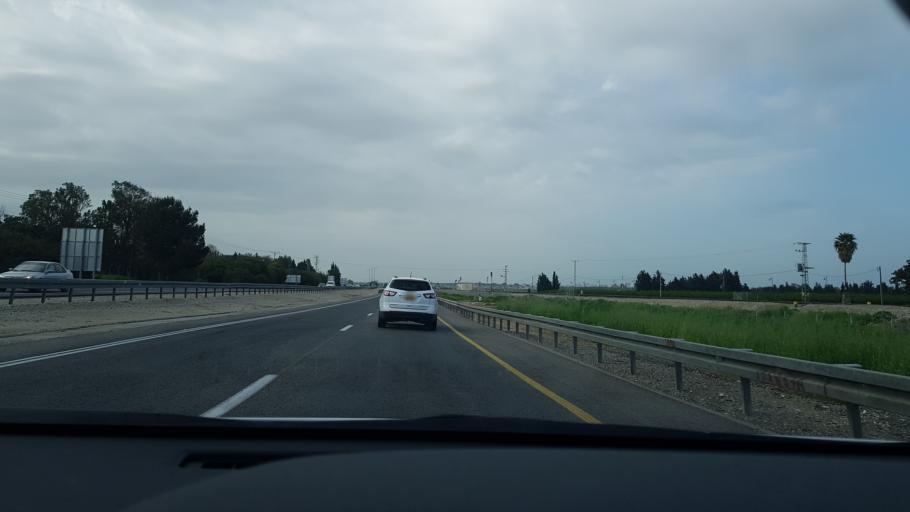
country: IL
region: Southern District
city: Ashdod
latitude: 31.7220
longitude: 34.6341
